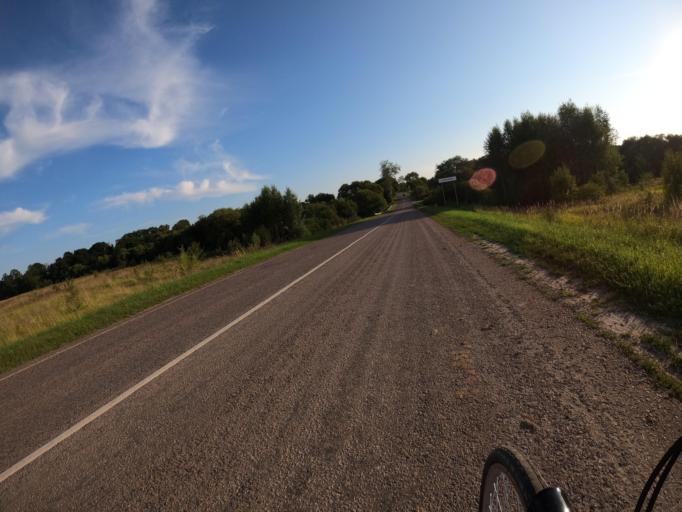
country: RU
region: Moskovskaya
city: Meshcherino
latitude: 55.1201
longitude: 38.3243
